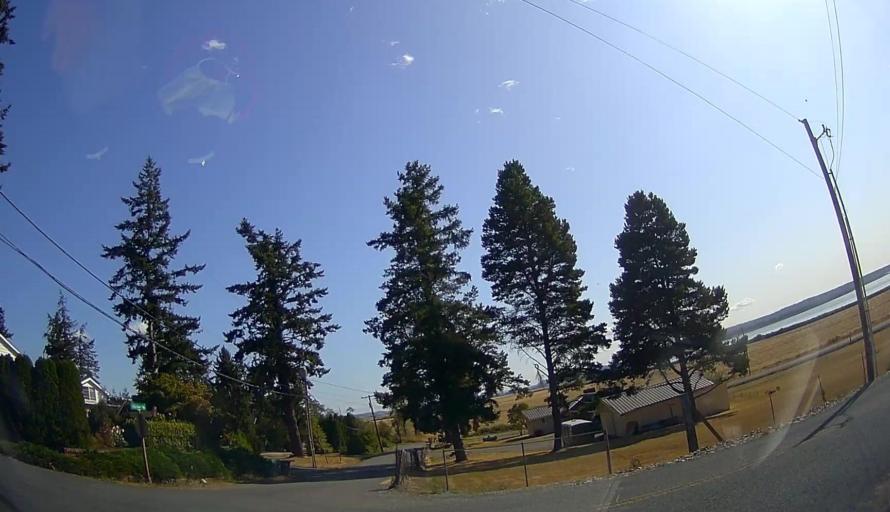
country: US
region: Washington
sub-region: Skagit County
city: Burlington
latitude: 48.4794
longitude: -122.4663
